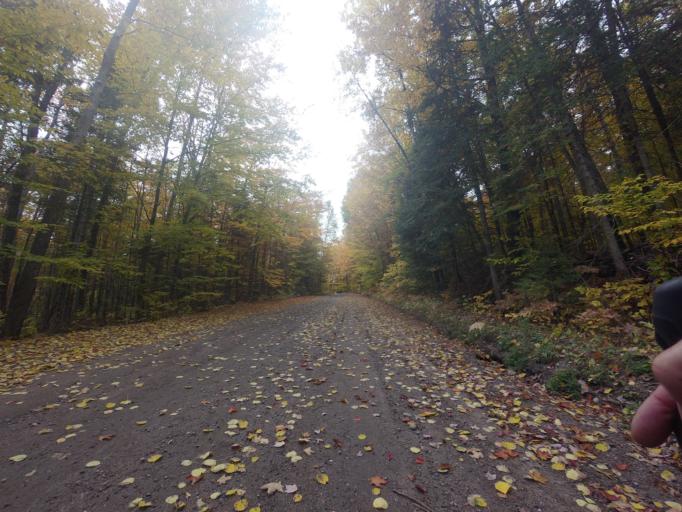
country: CA
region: Ontario
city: Pembroke
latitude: 45.7331
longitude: -77.2277
